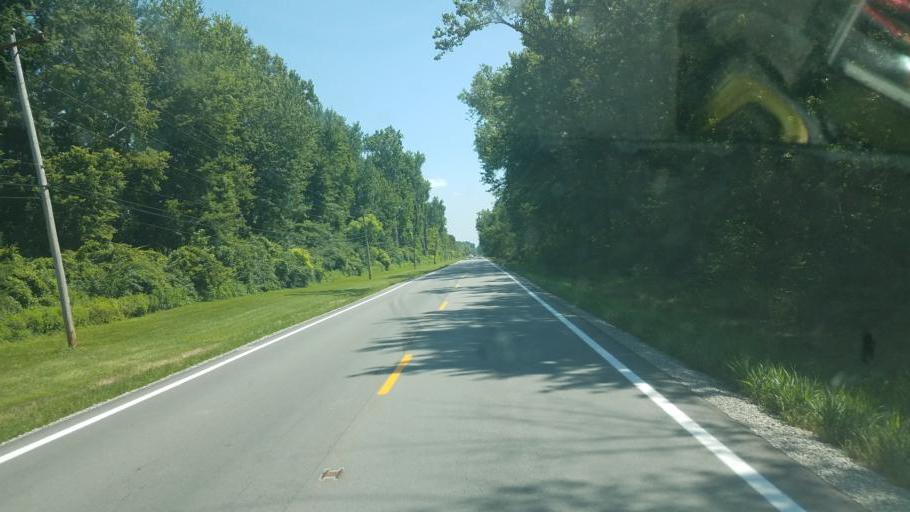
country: US
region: Ohio
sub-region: Erie County
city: Sandusky
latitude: 41.4244
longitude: -82.8195
